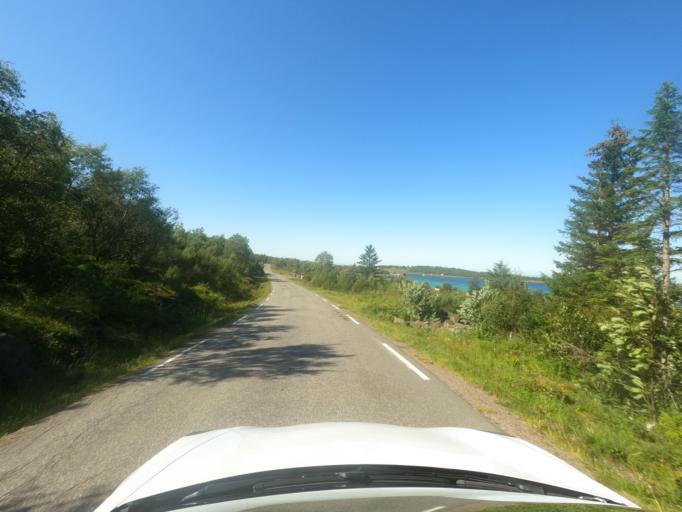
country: NO
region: Nordland
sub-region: Hadsel
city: Melbu
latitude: 68.4336
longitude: 14.7683
